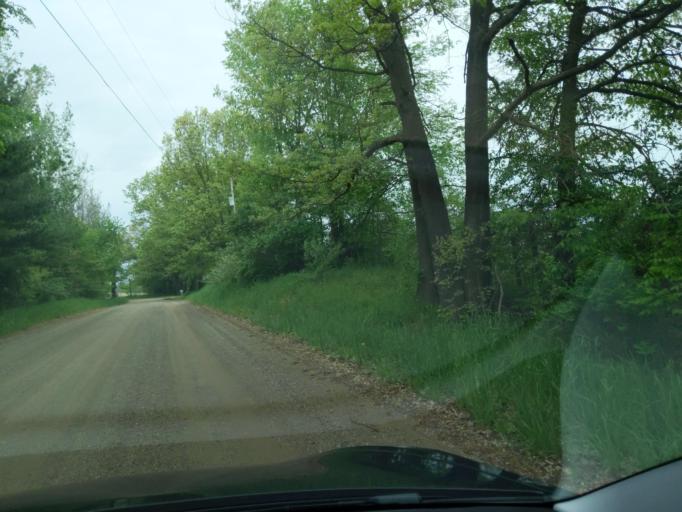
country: US
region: Michigan
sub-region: Ingham County
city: Stockbridge
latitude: 42.4064
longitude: -84.2102
